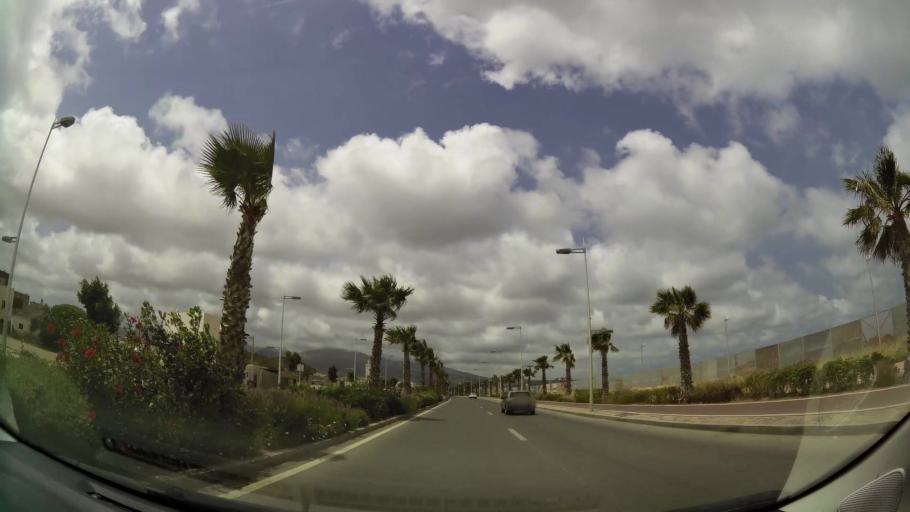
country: MA
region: Oriental
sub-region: Nador
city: Nador
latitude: 35.1698
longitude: -2.9147
